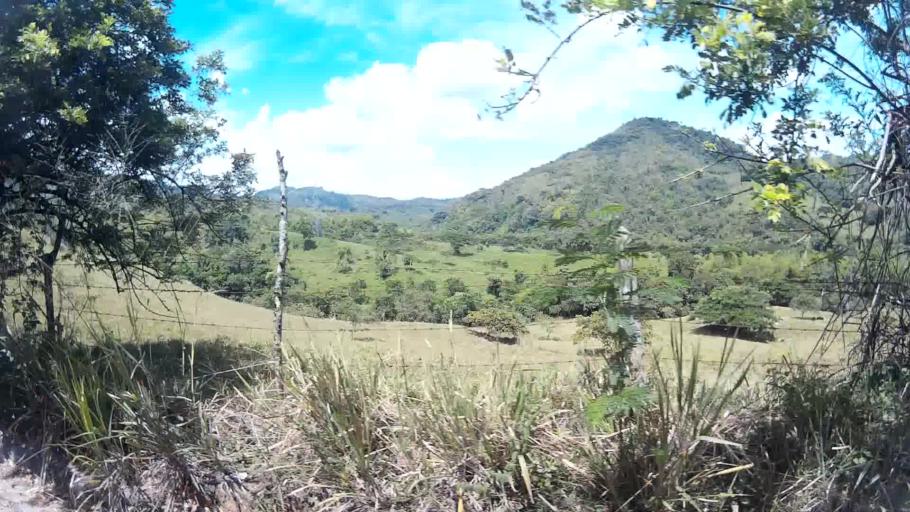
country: CO
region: Risaralda
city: La Virginia
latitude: 4.9349
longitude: -75.8496
